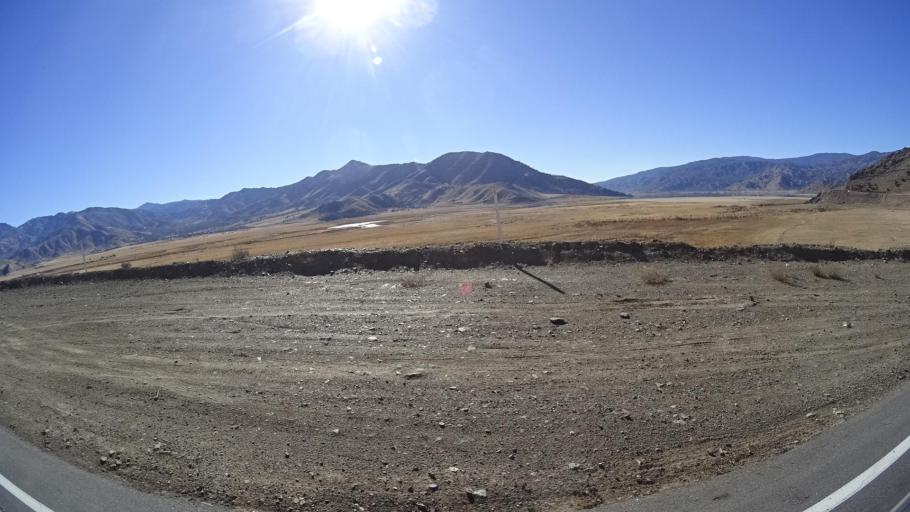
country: US
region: California
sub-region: Kern County
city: Wofford Heights
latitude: 35.6768
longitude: -118.4054
